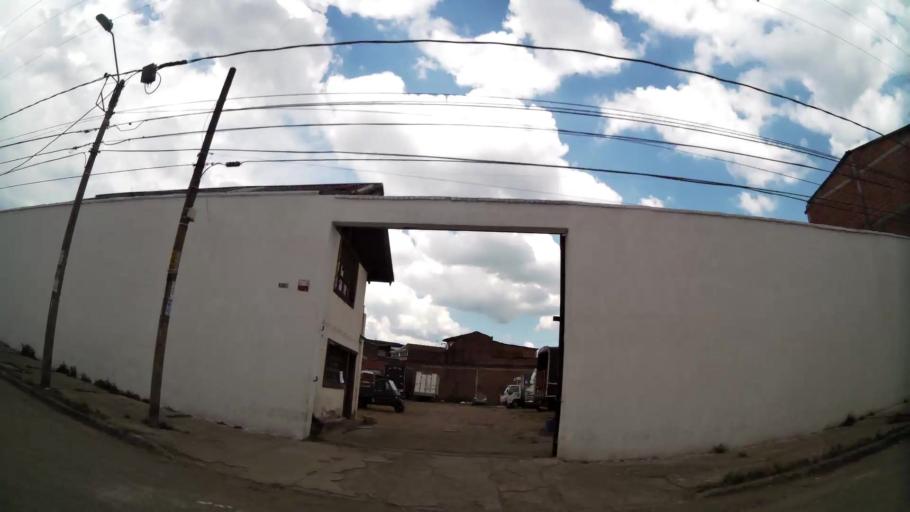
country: CO
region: Valle del Cauca
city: Cali
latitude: 3.4403
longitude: -76.5136
